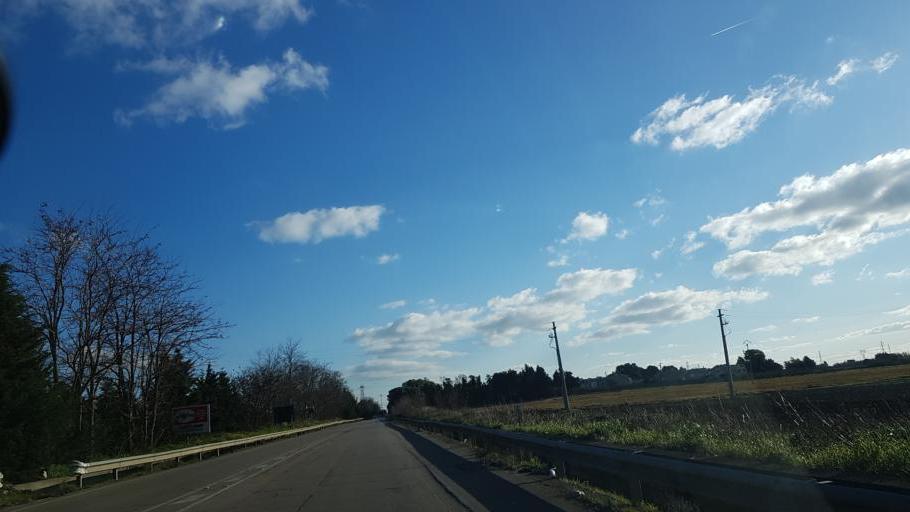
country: IT
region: Apulia
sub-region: Provincia di Brindisi
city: La Rosa
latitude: 40.6143
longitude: 17.9521
